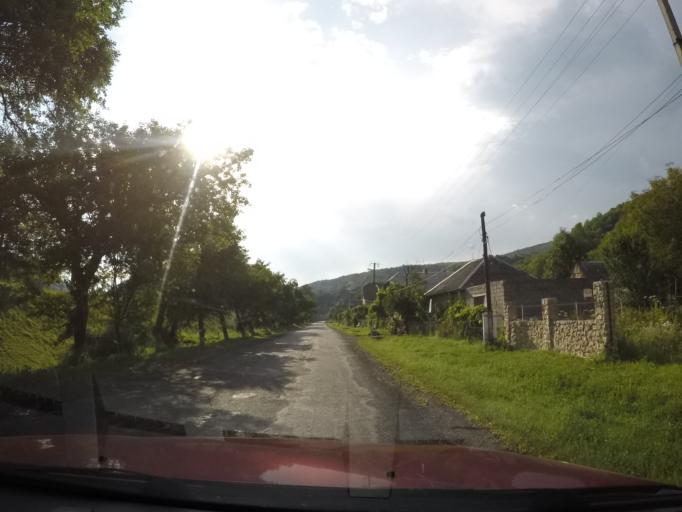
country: UA
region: Zakarpattia
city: Velykyi Bereznyi
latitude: 48.9521
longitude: 22.5339
